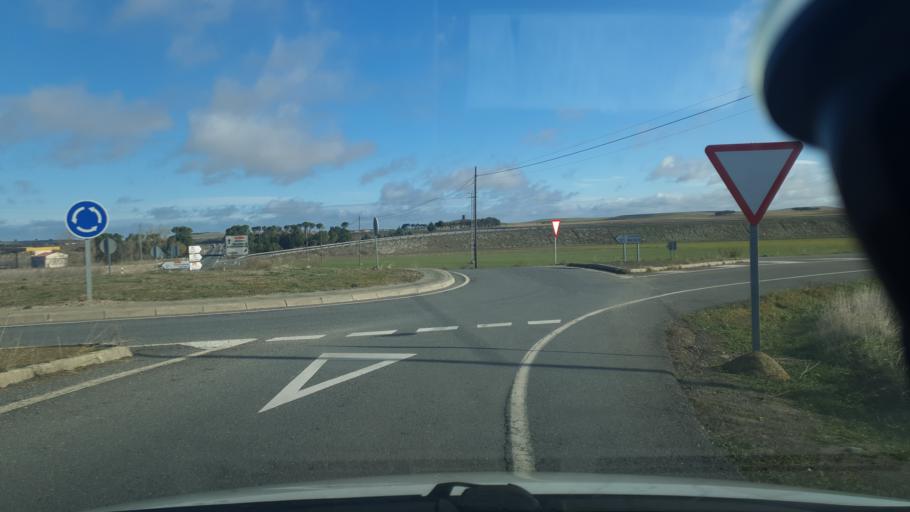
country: ES
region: Castille and Leon
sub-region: Provincia de Segovia
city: Codorniz
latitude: 41.0487
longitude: -4.6274
